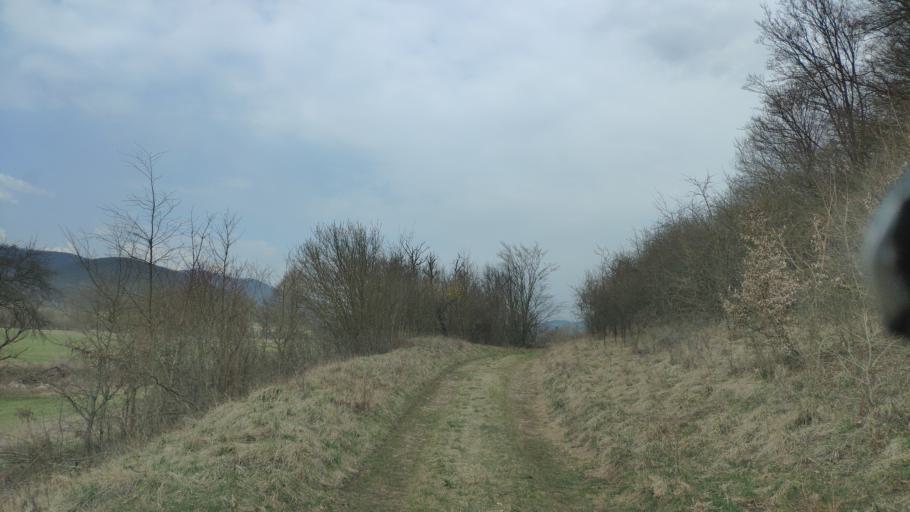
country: SK
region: Kosicky
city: Roznava
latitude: 48.6221
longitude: 20.3881
